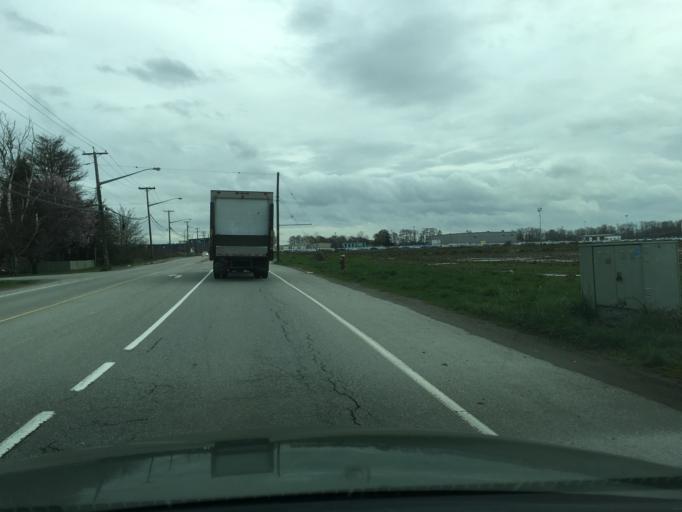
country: CA
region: British Columbia
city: Ladner
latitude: 49.1335
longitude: -123.0759
